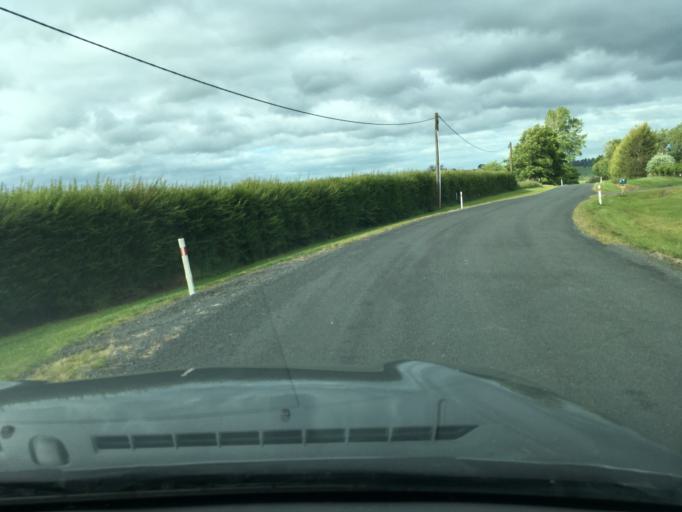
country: NZ
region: Waikato
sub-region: Hamilton City
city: Hamilton
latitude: -37.8230
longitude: 175.1746
